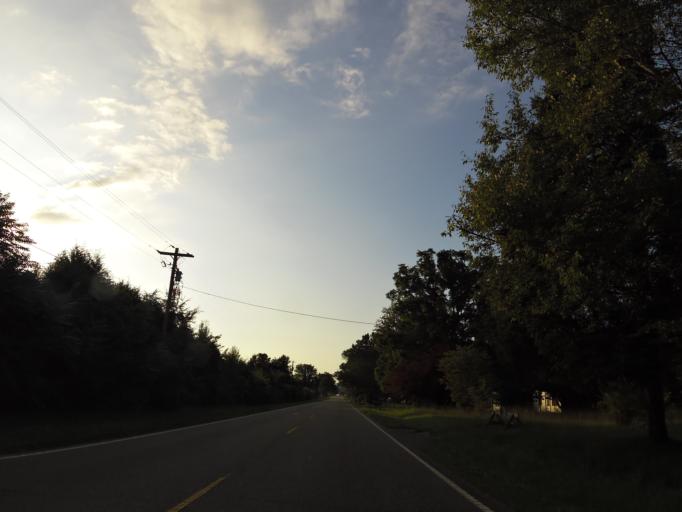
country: US
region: Tennessee
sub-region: Cocke County
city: Newport
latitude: 35.9809
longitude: -83.2796
